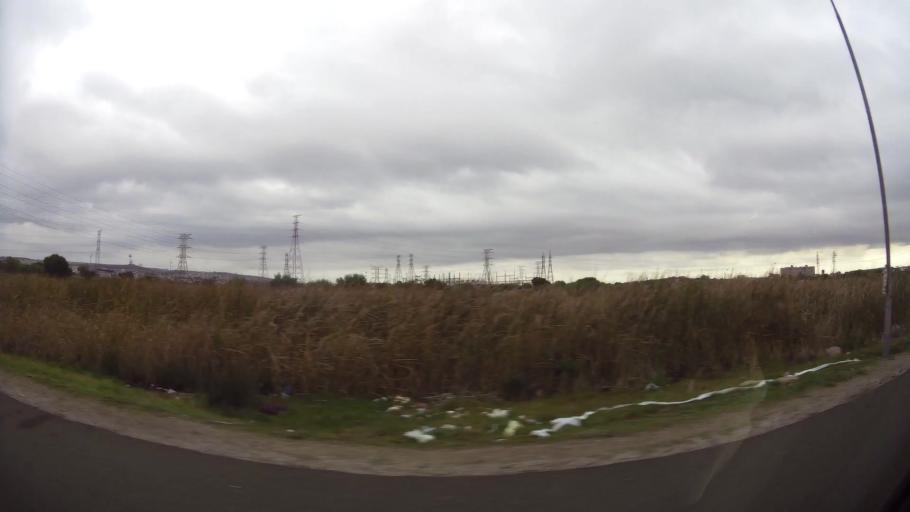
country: ZA
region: Eastern Cape
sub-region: Nelson Mandela Bay Metropolitan Municipality
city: Port Elizabeth
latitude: -33.9146
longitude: 25.5700
